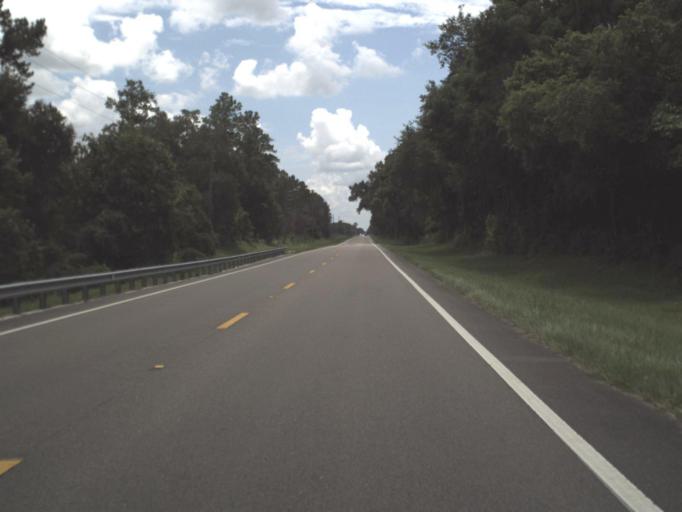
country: US
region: Florida
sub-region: Alachua County
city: Archer
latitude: 29.4824
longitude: -82.4891
